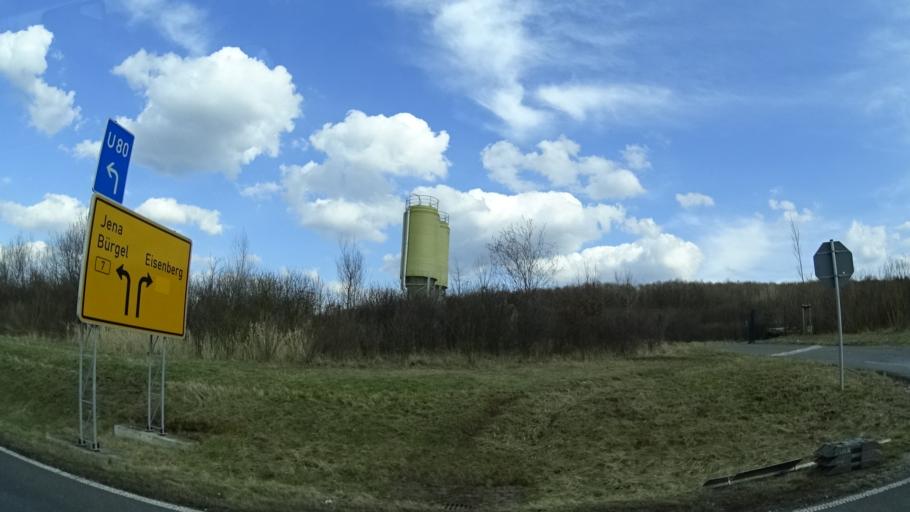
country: DE
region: Thuringia
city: Petersberg
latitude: 50.9697
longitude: 11.8599
